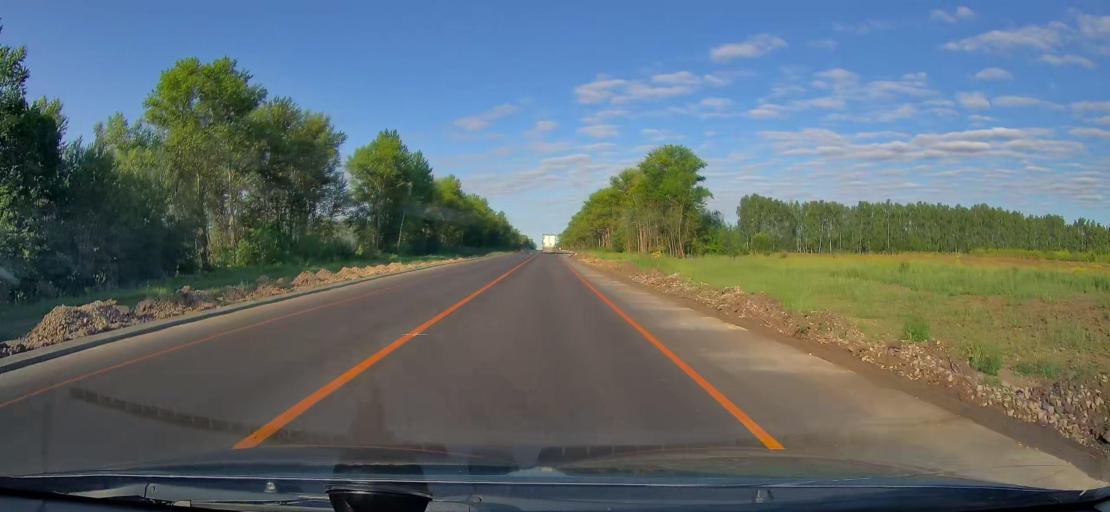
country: RU
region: Tula
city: Bol'shoye Skuratovo
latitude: 53.4400
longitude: 36.8236
